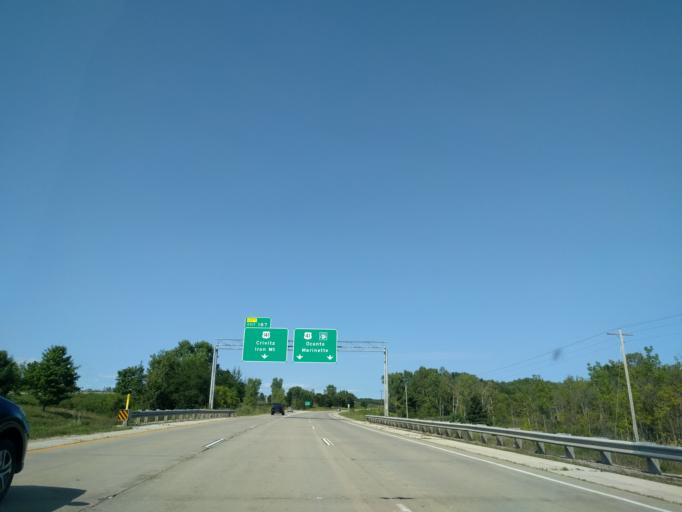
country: US
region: Wisconsin
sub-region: Oconto County
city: Oconto Falls
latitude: 44.7852
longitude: -88.0461
